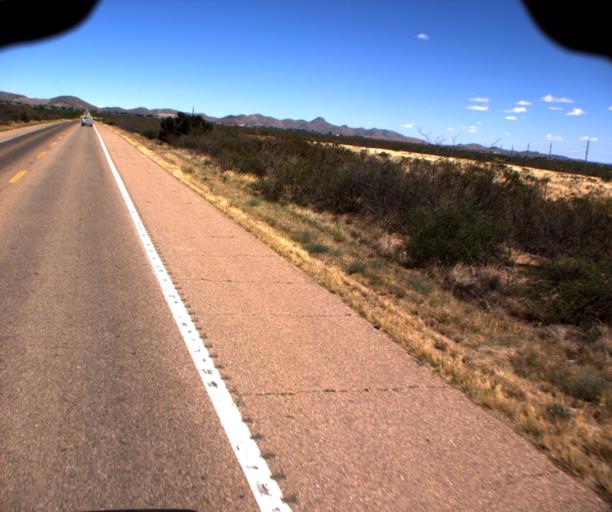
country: US
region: Arizona
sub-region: Cochise County
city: Naco
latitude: 31.3806
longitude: -109.9601
